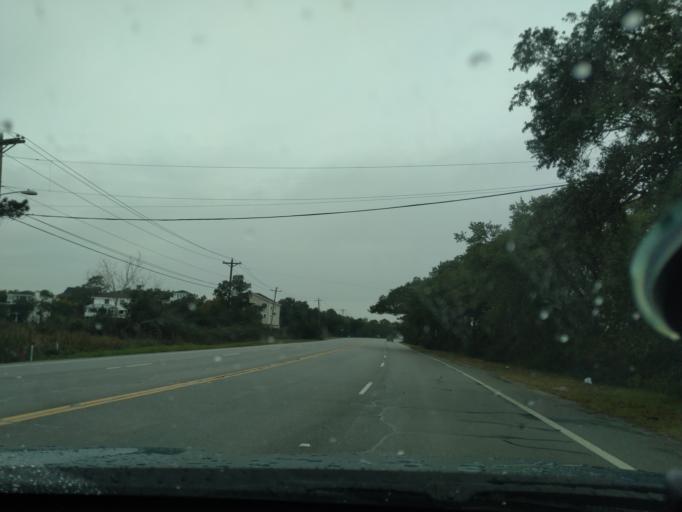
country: US
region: South Carolina
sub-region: Charleston County
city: Folly Beach
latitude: 32.6880
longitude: -79.9611
